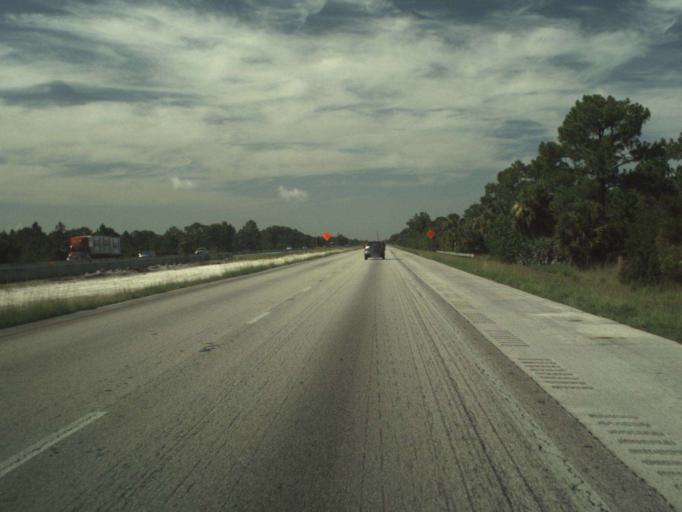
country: US
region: Florida
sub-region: Indian River County
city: Fellsmere
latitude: 27.7920
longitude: -80.5499
